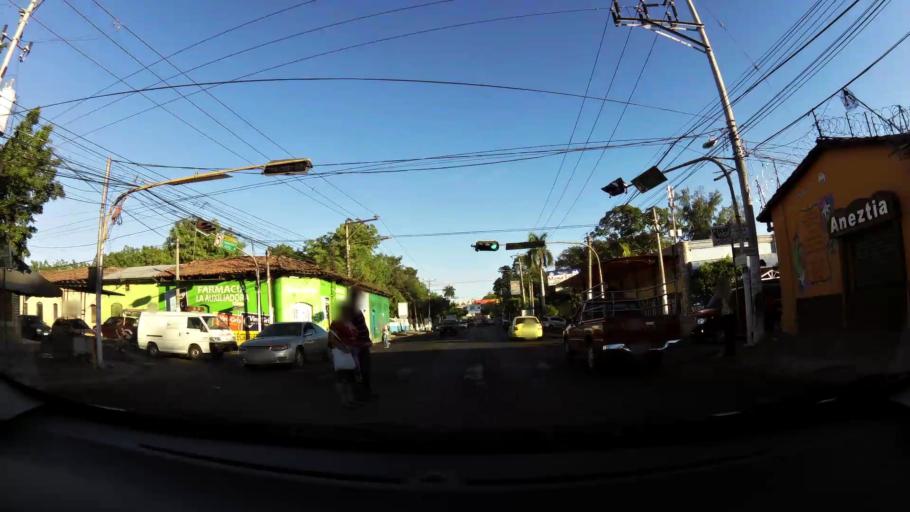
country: SV
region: San Miguel
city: San Miguel
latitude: 13.4807
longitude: -88.1849
